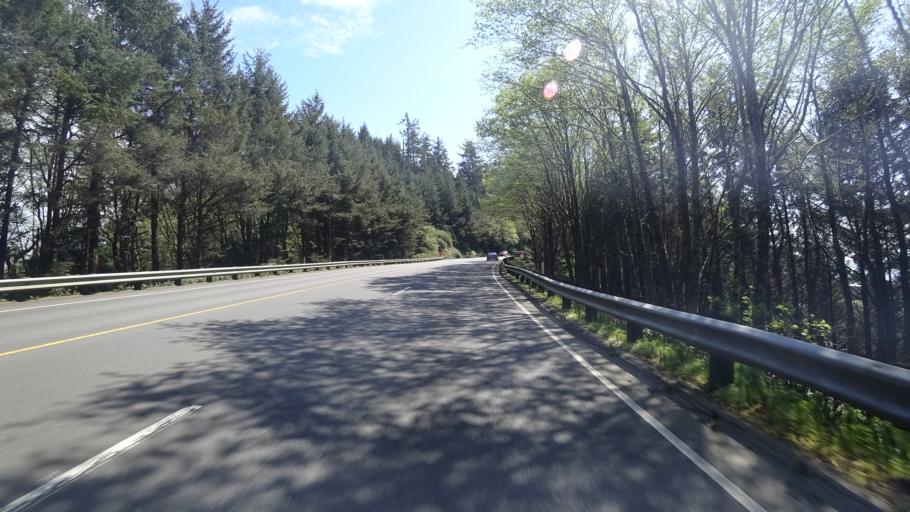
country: US
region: Oregon
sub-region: Lincoln County
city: Depoe Bay
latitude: 44.7784
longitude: -124.0704
